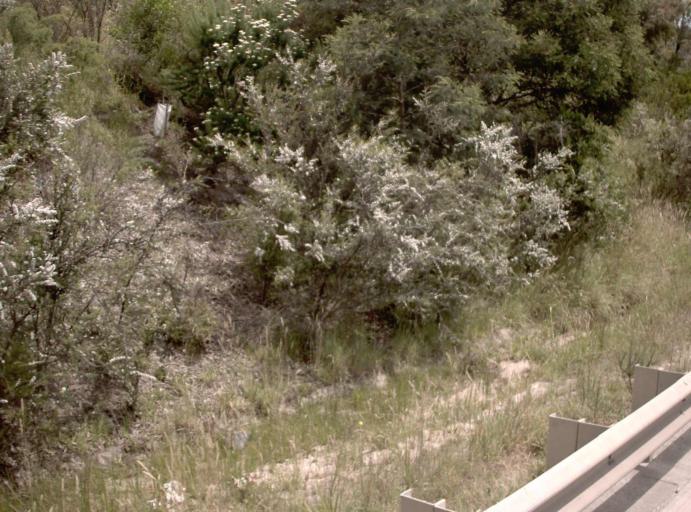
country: AU
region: Victoria
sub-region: Casey
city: Cranbourne South
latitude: -38.1679
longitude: 145.2217
